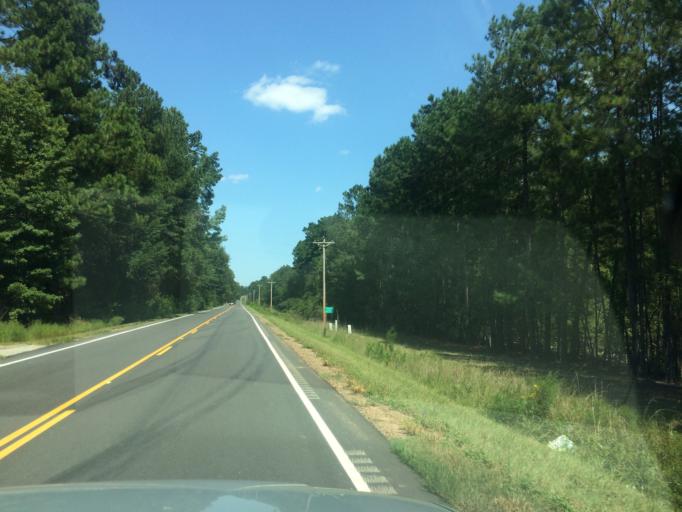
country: US
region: South Carolina
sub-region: Barnwell County
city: Williston
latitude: 33.5740
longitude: -81.5203
